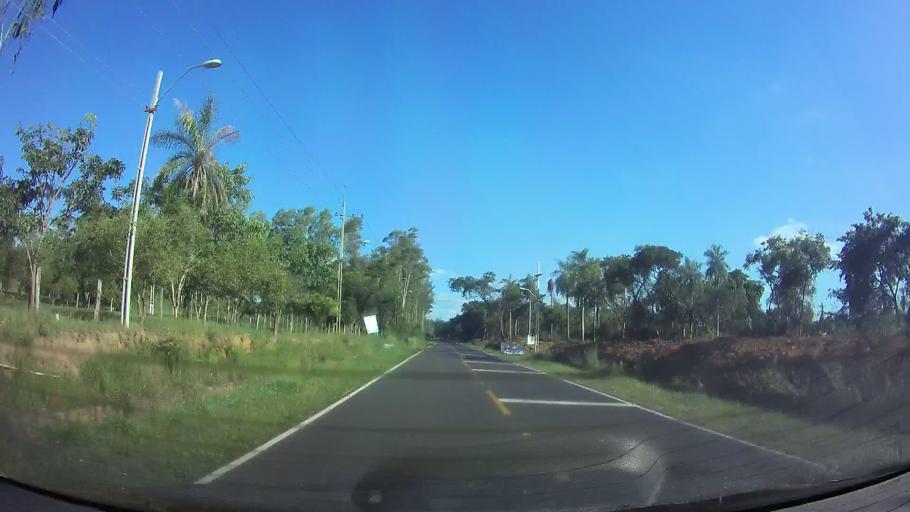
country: PY
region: Cordillera
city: Atyra
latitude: -25.3012
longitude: -57.1603
